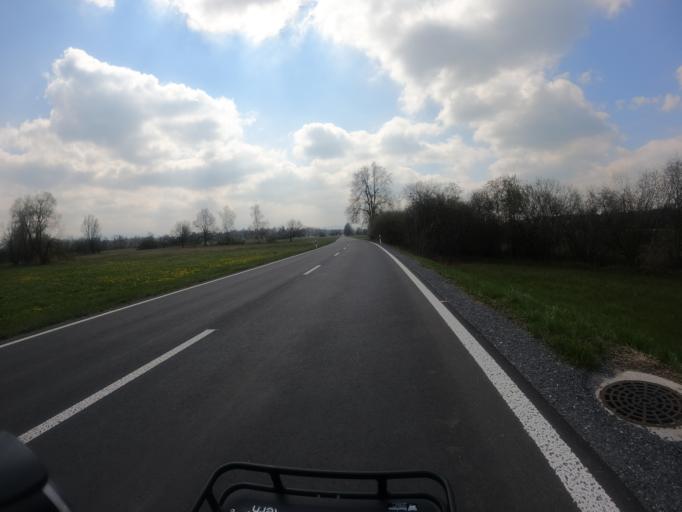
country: CH
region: Zurich
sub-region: Bezirk Affoltern
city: Obfelden / Oberlunnern
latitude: 47.2299
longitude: 8.4152
